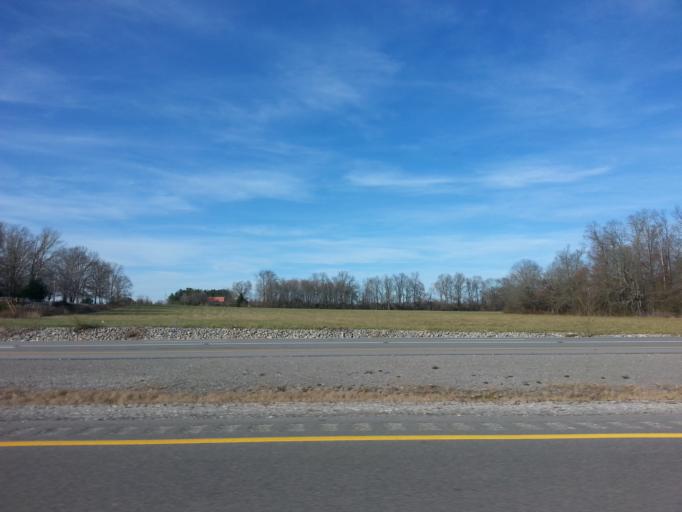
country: US
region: Tennessee
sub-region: Warren County
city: McMinnville
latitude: 35.7192
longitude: -85.8718
